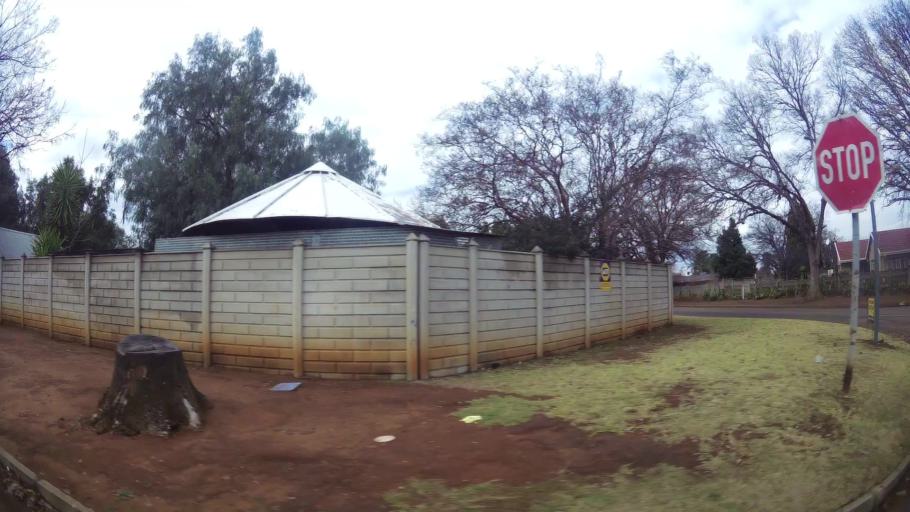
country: ZA
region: Gauteng
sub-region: Sedibeng District Municipality
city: Vereeniging
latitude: -26.6454
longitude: 27.9749
